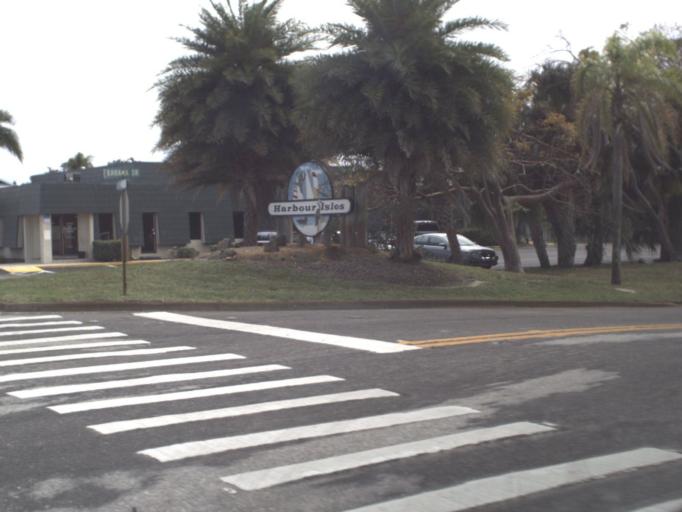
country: US
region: Florida
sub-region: Brevard County
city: Indian Harbour Beach
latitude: 28.1486
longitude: -80.5995
